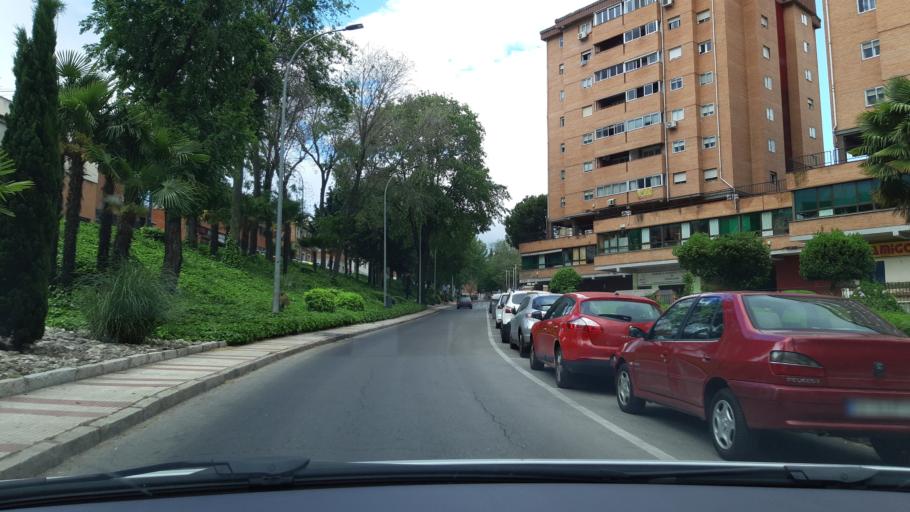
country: ES
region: Castille-La Mancha
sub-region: Provincia de Guadalajara
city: Guadalajara
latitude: 40.6317
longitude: -3.1691
